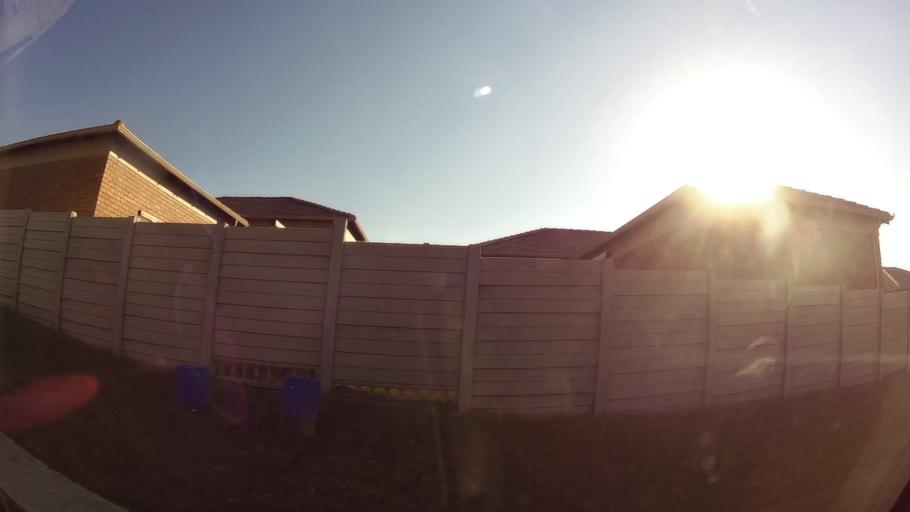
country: ZA
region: Gauteng
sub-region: City of Johannesburg Metropolitan Municipality
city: Midrand
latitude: -25.9089
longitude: 28.1120
